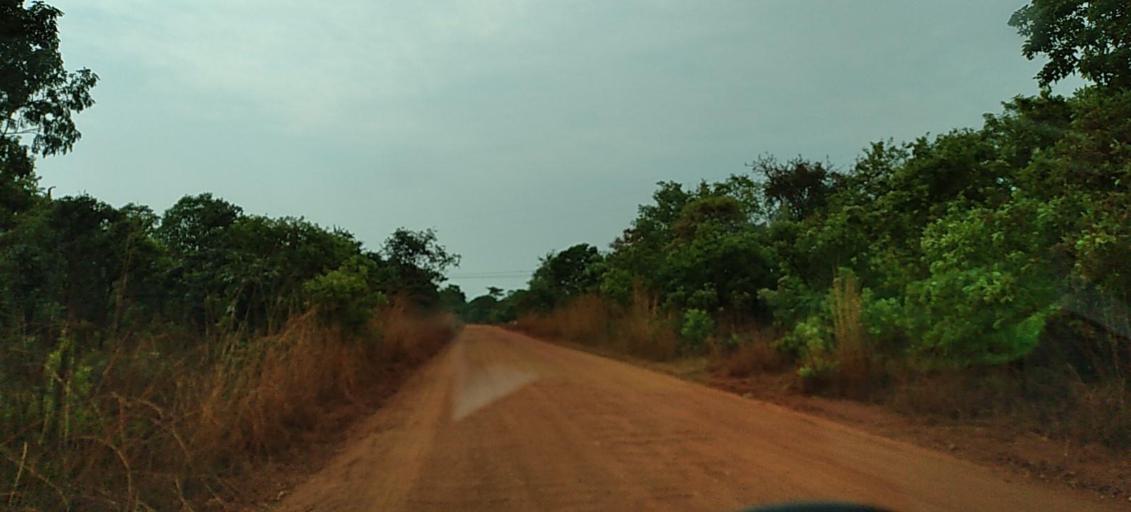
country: ZM
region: North-Western
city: Solwezi
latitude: -12.2138
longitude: 26.5050
